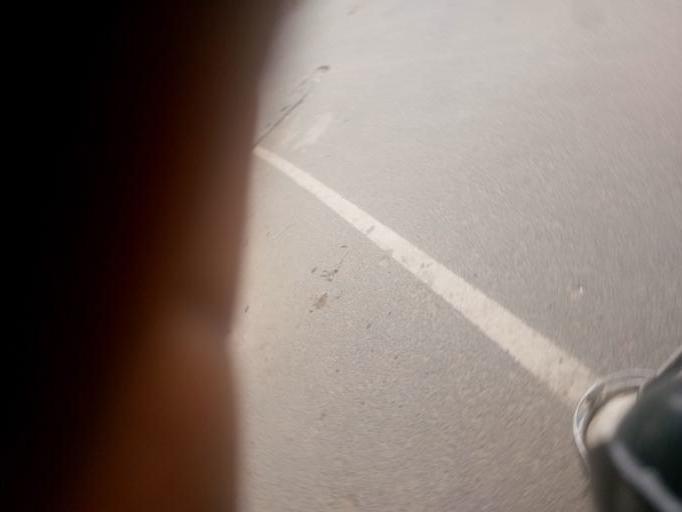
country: IN
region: Karnataka
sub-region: Bangalore Urban
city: Bangalore
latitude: 13.0123
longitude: 77.6278
